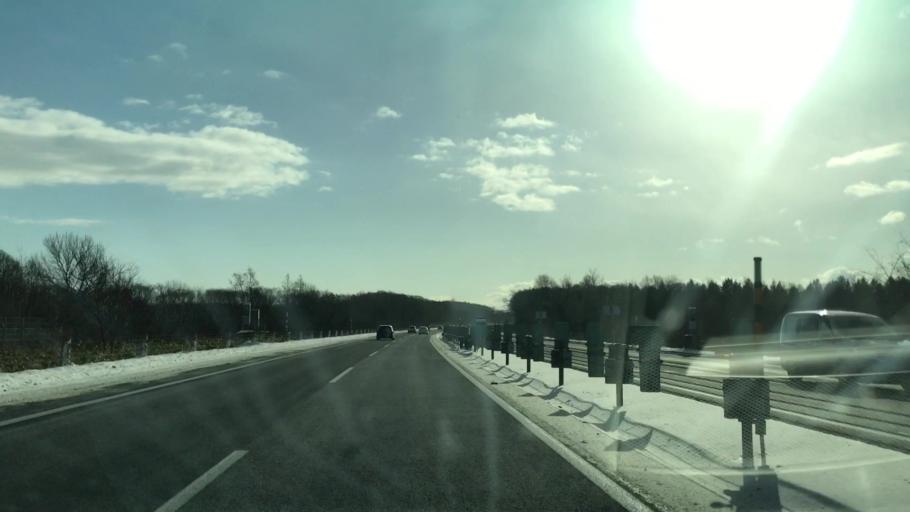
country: JP
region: Hokkaido
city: Chitose
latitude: 42.8368
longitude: 141.6055
